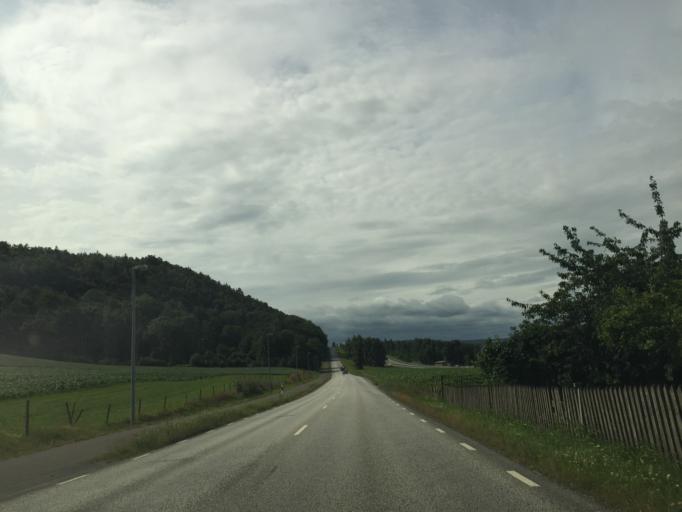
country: SE
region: Joenkoeping
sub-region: Jonkopings Kommun
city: Kaxholmen
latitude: 57.8338
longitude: 14.2718
